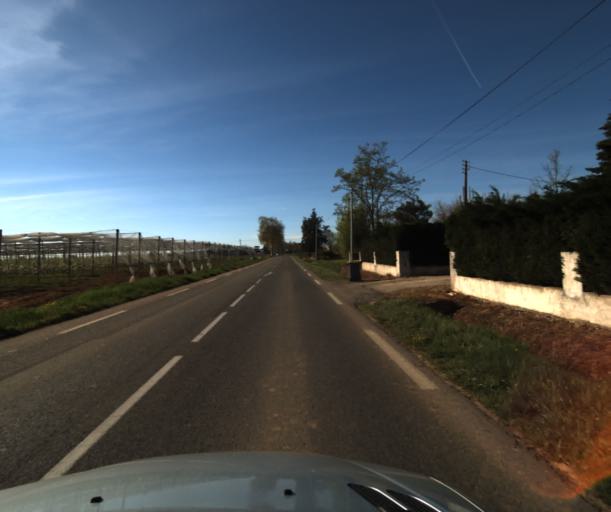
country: FR
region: Midi-Pyrenees
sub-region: Departement du Tarn-et-Garonne
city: Montbeton
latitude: 44.0385
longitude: 1.3082
